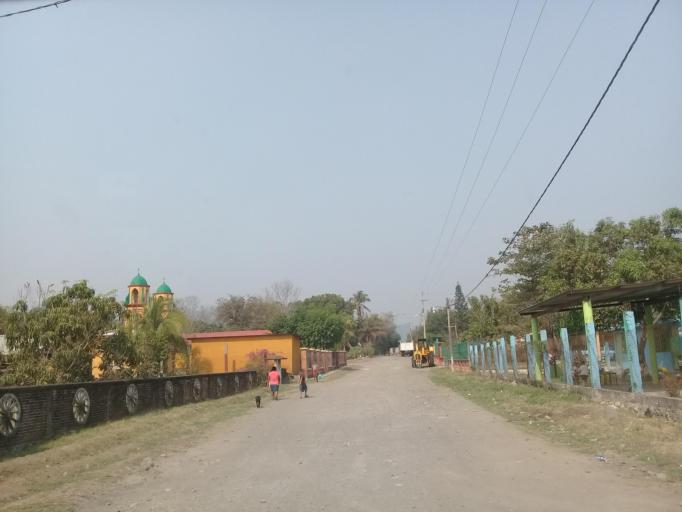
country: MX
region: Oaxaca
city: Acatlan de Perez Figueroa
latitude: 18.6059
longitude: -96.5768
